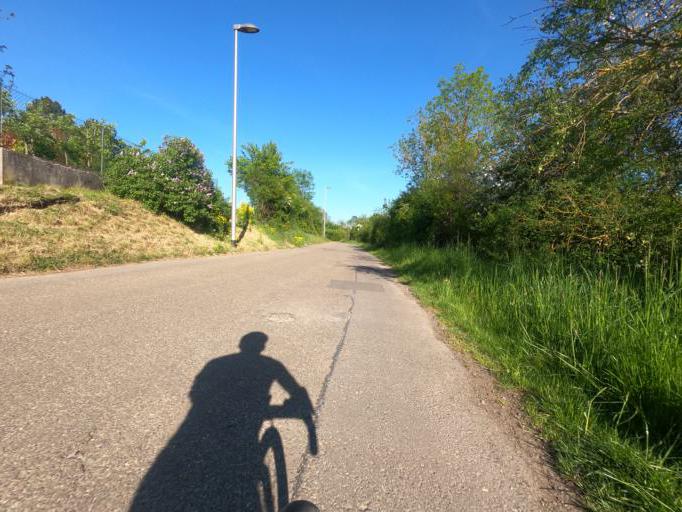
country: DE
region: Baden-Wuerttemberg
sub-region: Regierungsbezirk Stuttgart
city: Aidlingen
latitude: 48.7099
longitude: 8.9198
